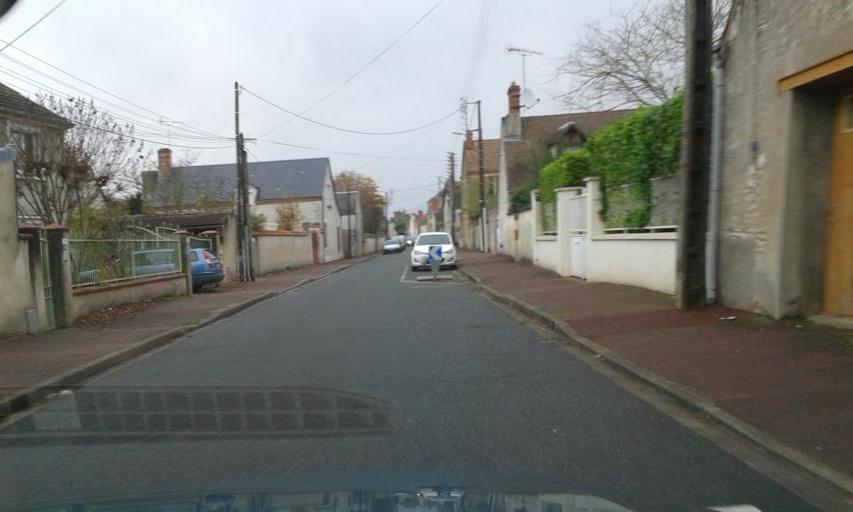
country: FR
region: Centre
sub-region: Departement du Loiret
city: Olivet
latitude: 47.8592
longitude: 1.8994
